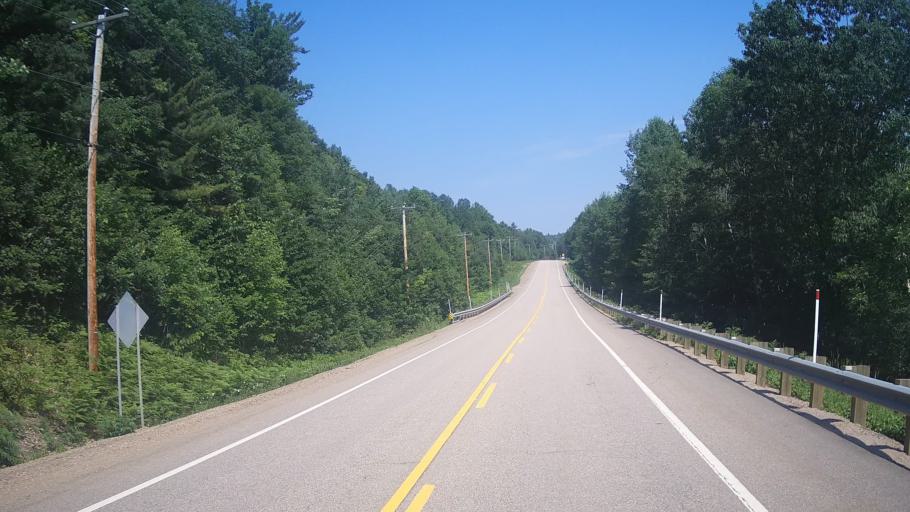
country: CA
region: Ontario
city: Pembroke
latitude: 45.9175
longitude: -76.9357
